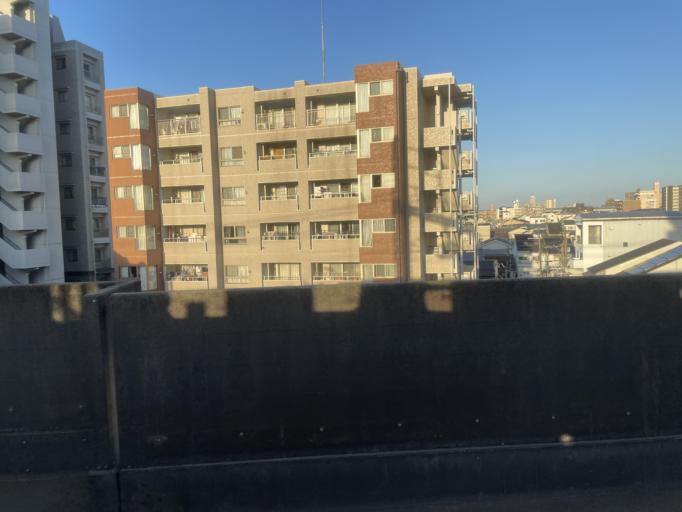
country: JP
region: Osaka
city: Matsubara
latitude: 34.6297
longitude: 135.5299
